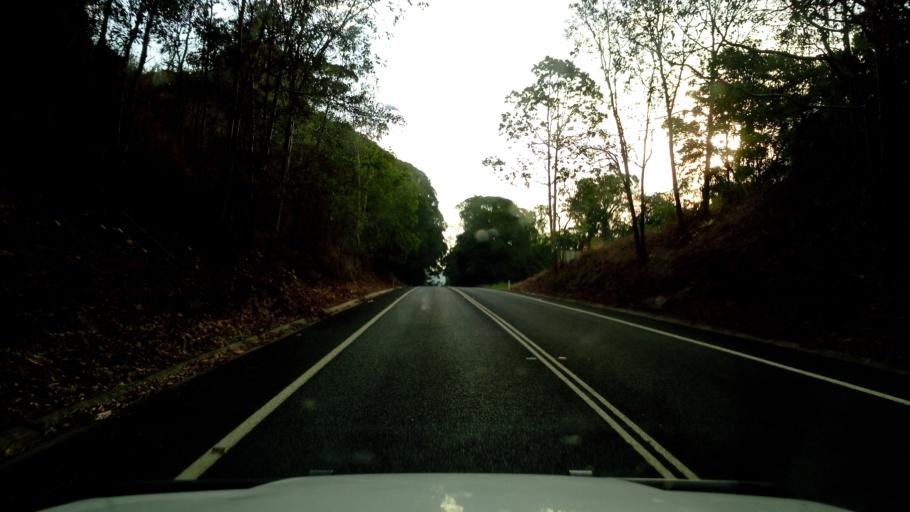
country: AU
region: Queensland
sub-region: Tablelands
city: Kuranda
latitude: -16.8423
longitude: 145.6105
